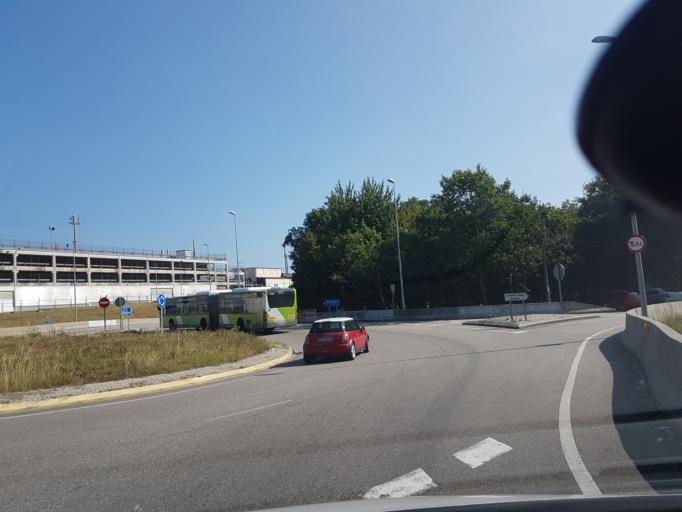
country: ES
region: Galicia
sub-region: Provincia de Pontevedra
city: Redondela
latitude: 42.2286
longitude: -8.6332
